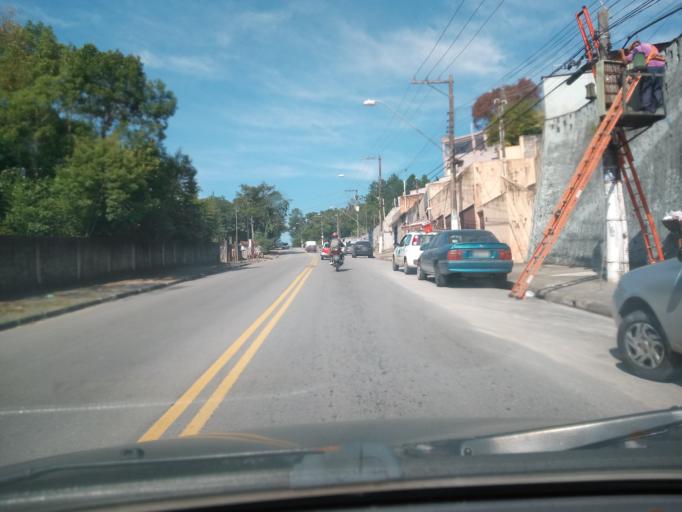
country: BR
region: Sao Paulo
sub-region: Sao Bernardo Do Campo
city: Sao Bernardo do Campo
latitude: -23.7915
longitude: -46.5389
